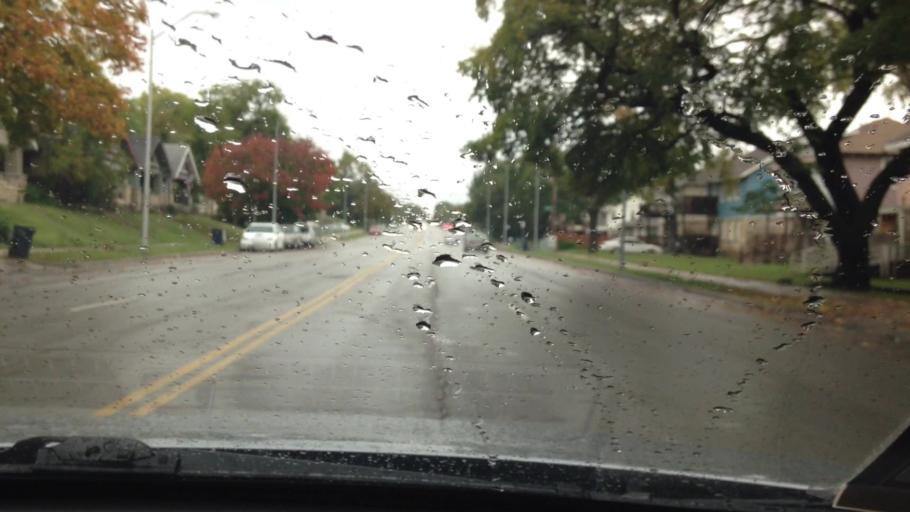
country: US
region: Kansas
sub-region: Johnson County
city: Westwood
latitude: 39.0477
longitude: -94.5679
